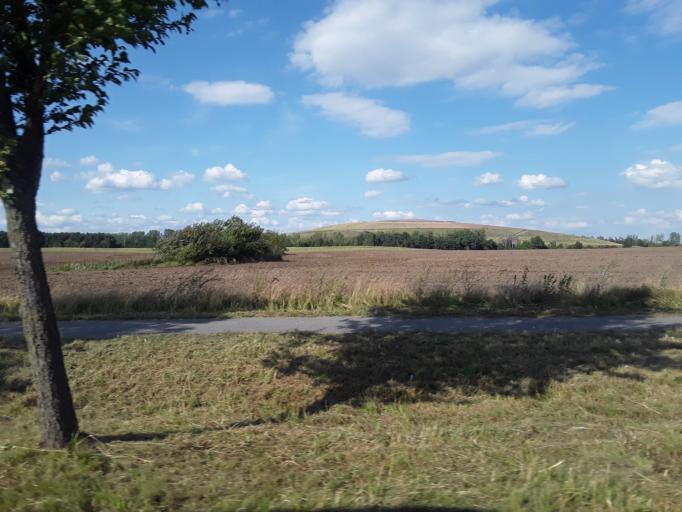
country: DE
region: Berlin
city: Buch
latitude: 52.6274
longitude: 13.5344
